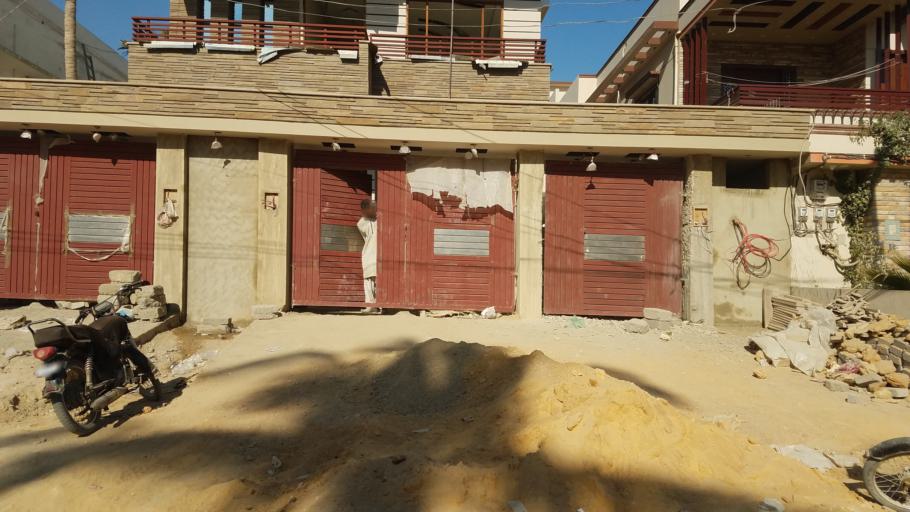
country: PK
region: Sindh
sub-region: Karachi District
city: Karachi
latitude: 24.9249
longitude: 67.0504
